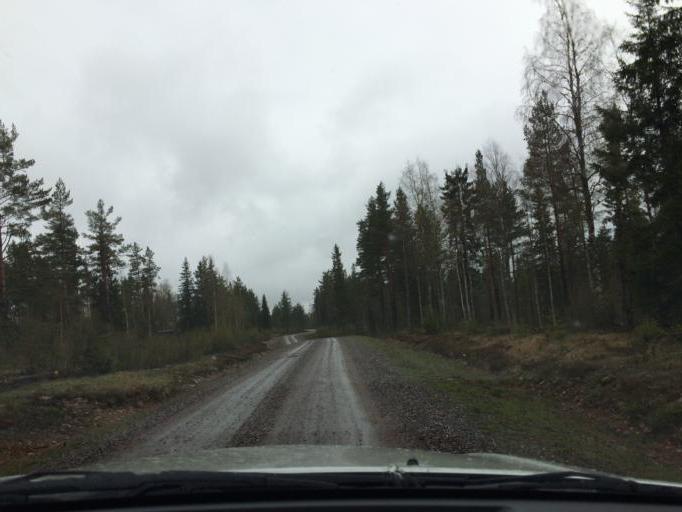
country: SE
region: OErebro
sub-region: Hallefors Kommun
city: Haellefors
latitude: 60.0373
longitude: 14.5305
